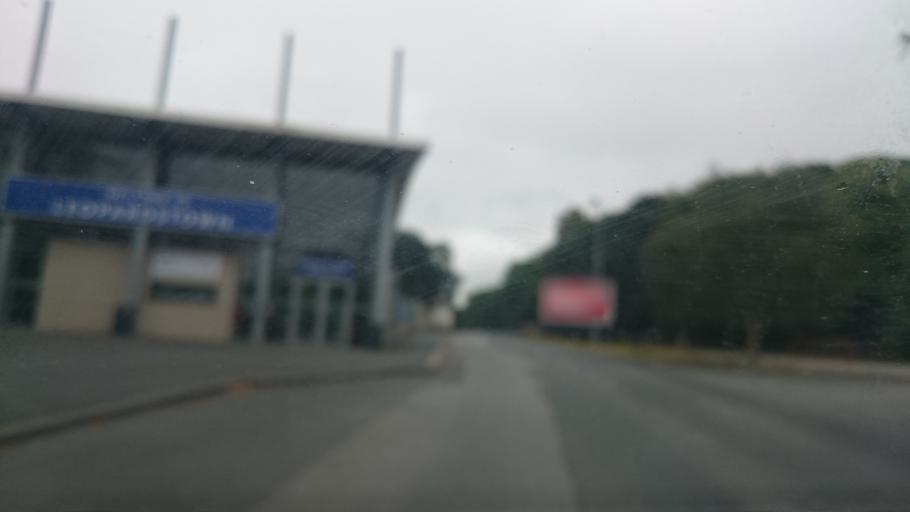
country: IE
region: Leinster
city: Foxrock
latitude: 53.2672
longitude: -6.1956
